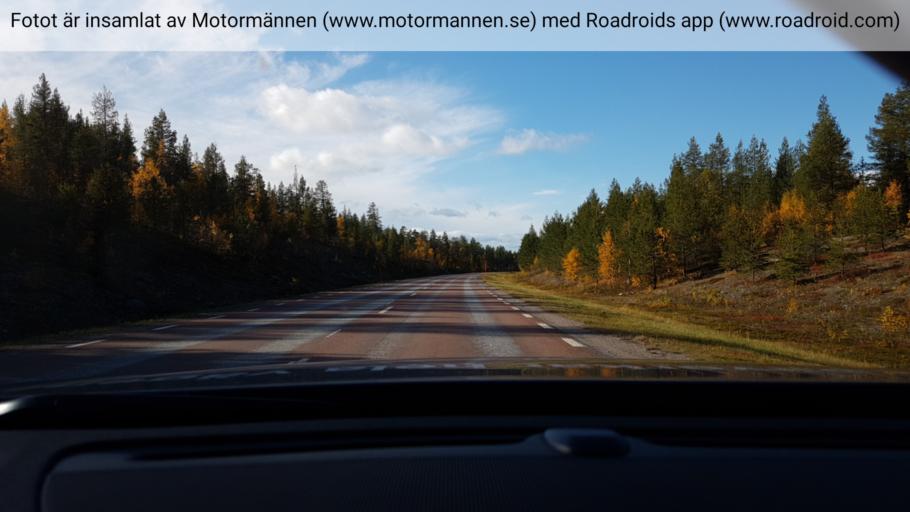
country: SE
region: Norrbotten
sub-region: Arjeplogs Kommun
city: Arjeplog
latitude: 66.0534
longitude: 17.9221
